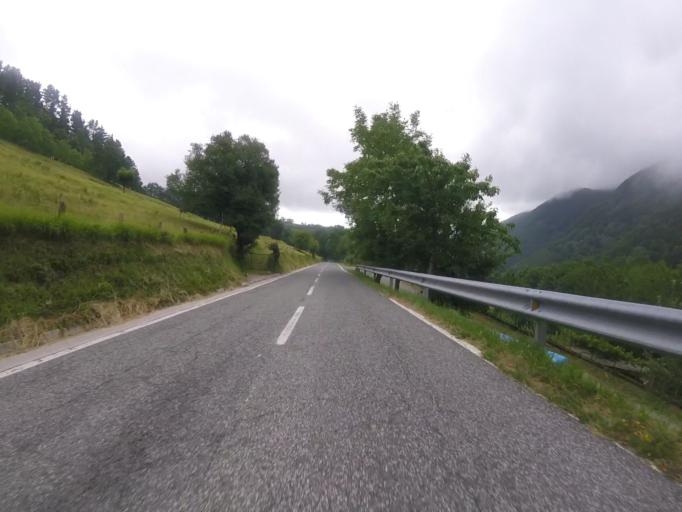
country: ES
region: Navarre
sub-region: Provincia de Navarra
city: Ezkurra
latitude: 43.0850
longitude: -1.8487
